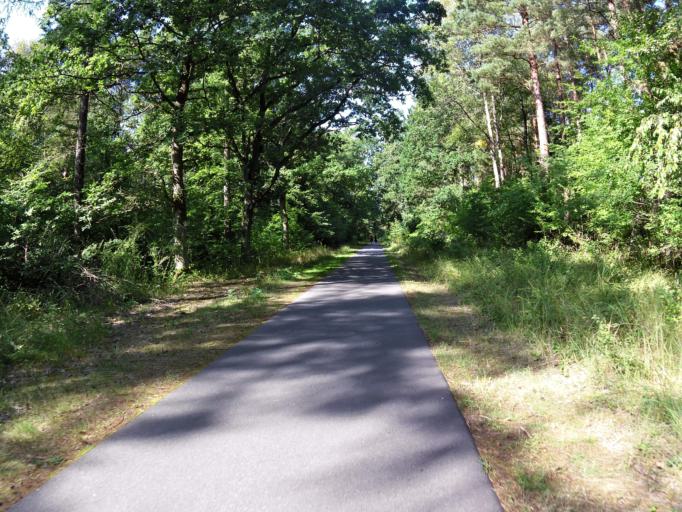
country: DE
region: Mecklenburg-Vorpommern
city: Karlshagen
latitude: 54.1265
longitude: 13.8217
